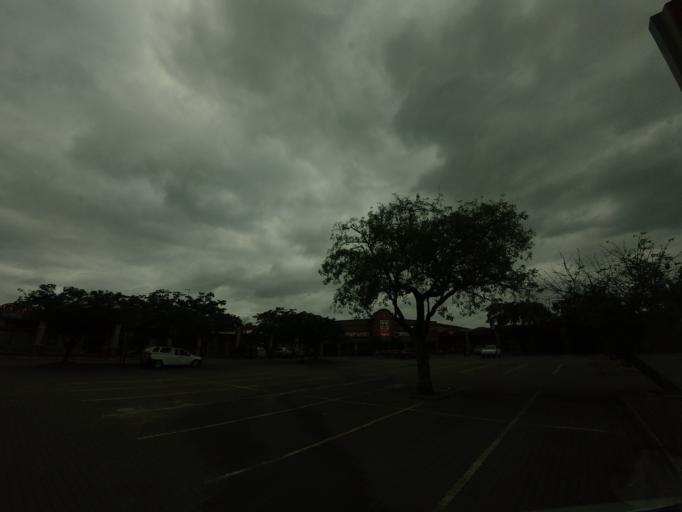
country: ZA
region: Mpumalanga
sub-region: Ehlanzeni District
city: Komatipoort
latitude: -25.4377
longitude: 31.9607
